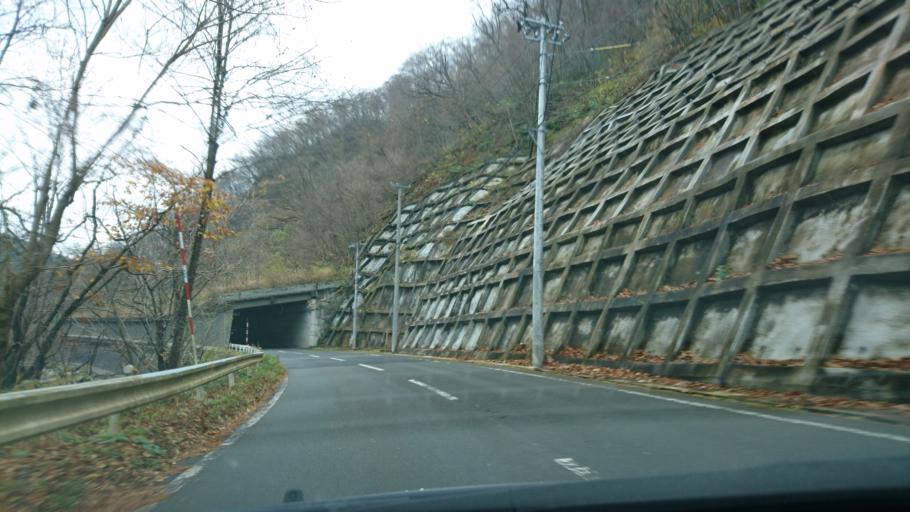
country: JP
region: Iwate
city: Ichinoseki
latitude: 38.9090
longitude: 140.8833
